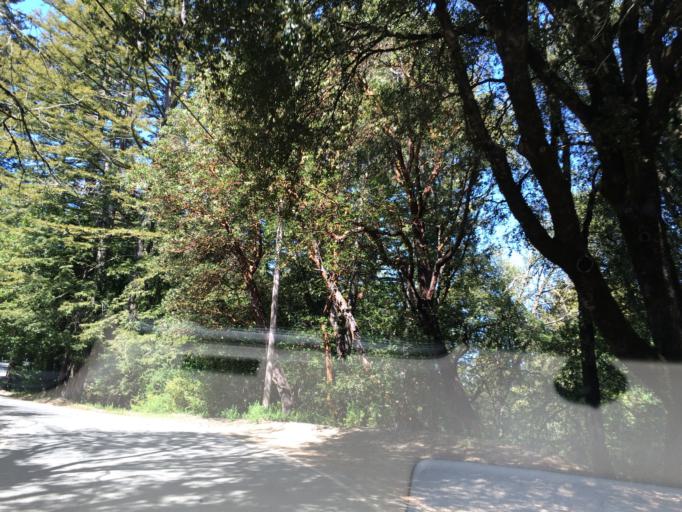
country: US
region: California
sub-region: Santa Clara County
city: Monte Sereno
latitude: 37.1899
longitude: -122.0308
